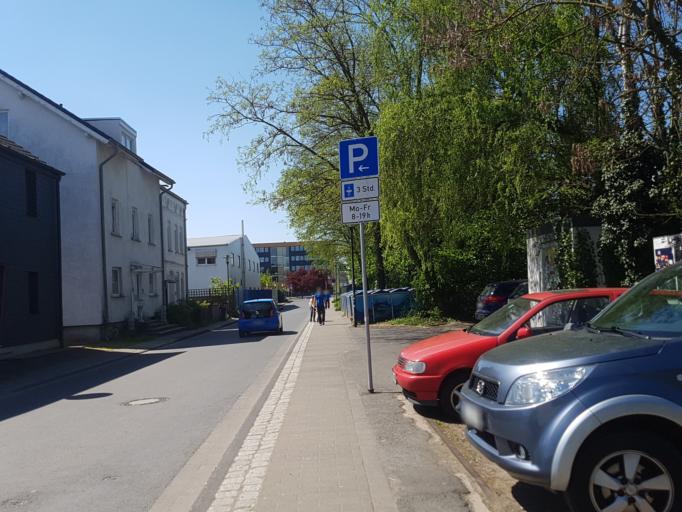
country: DE
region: North Rhine-Westphalia
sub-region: Regierungsbezirk Koln
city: Hennef
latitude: 50.7726
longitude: 7.2879
